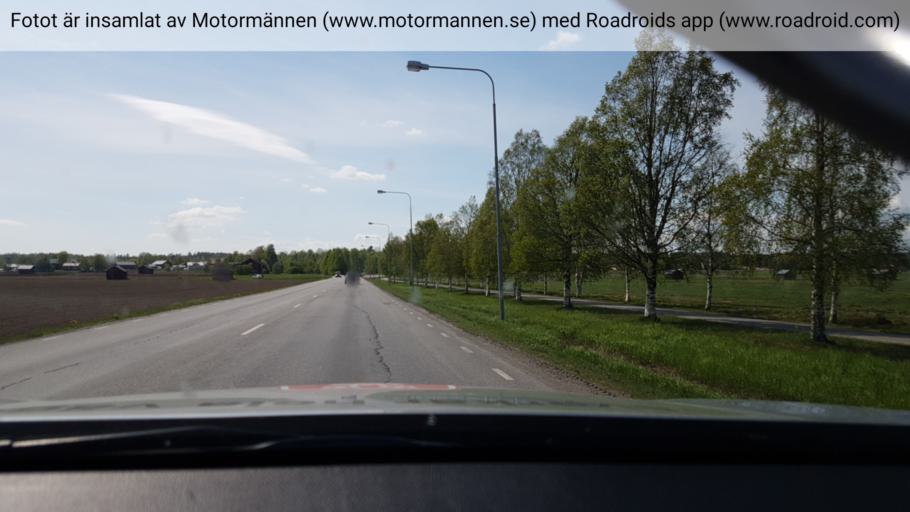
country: SE
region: Vaesterbotten
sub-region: Umea Kommun
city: Roback
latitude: 63.8126
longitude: 20.2128
